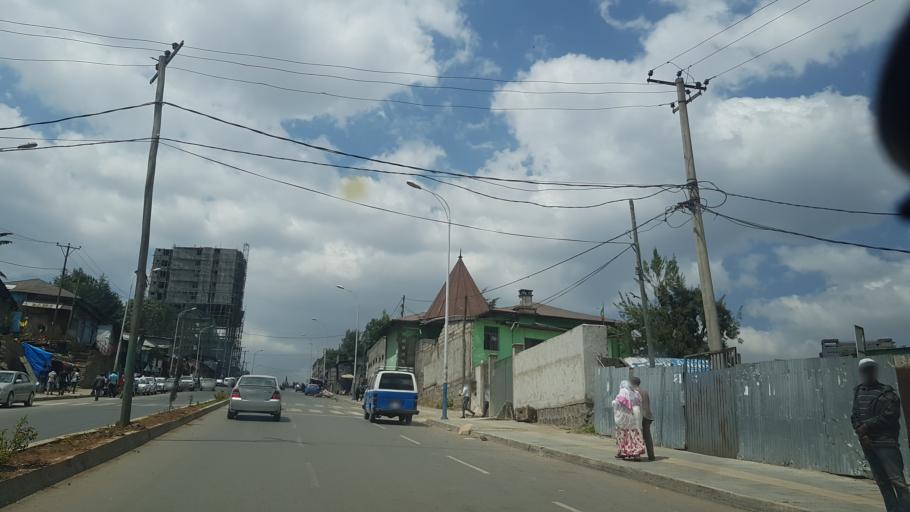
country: ET
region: Adis Abeba
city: Addis Ababa
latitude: 9.0281
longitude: 38.7483
